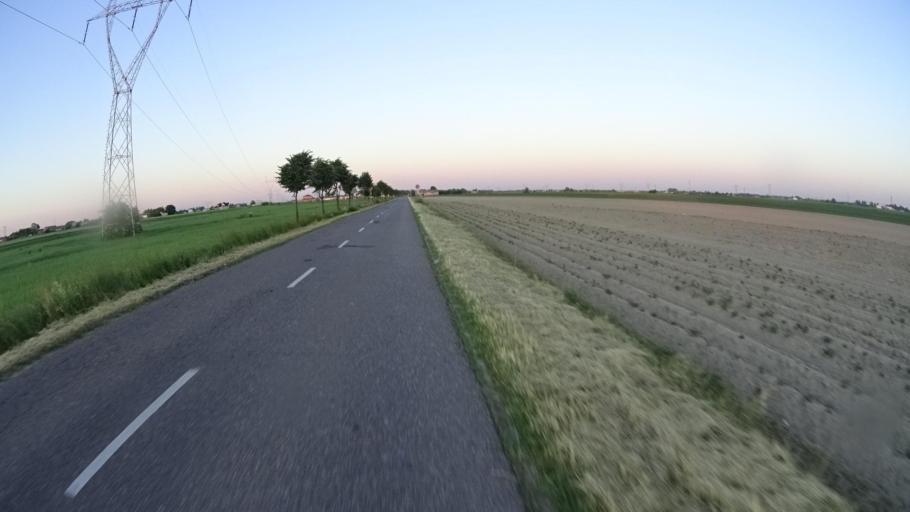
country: PL
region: Masovian Voivodeship
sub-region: Powiat warszawski zachodni
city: Jozefow
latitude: 52.2359
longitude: 20.6664
